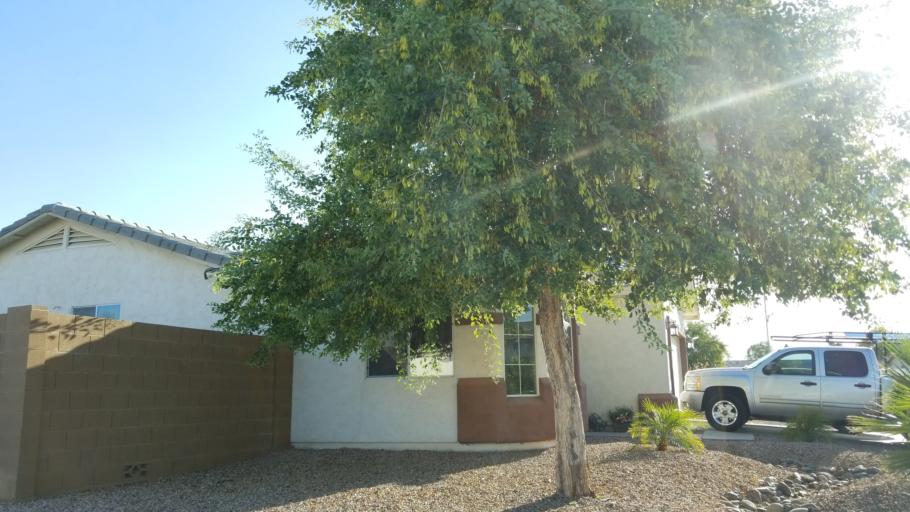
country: US
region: Arizona
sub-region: Maricopa County
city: Laveen
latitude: 33.3804
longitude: -112.2159
